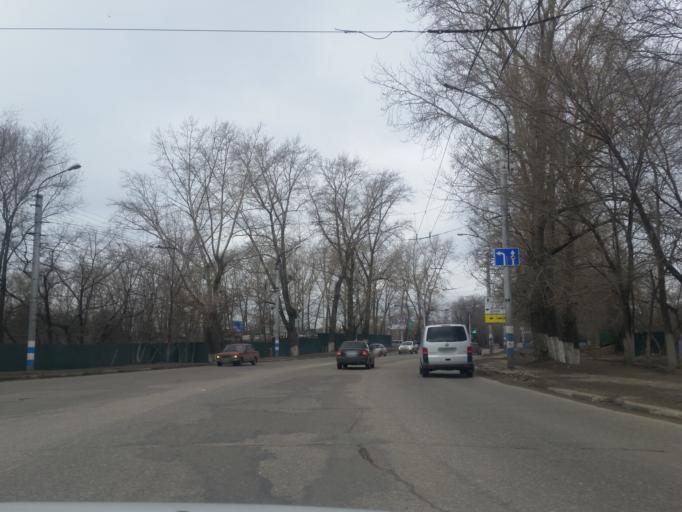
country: RU
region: Ulyanovsk
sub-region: Ulyanovskiy Rayon
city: Ulyanovsk
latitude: 54.3297
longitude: 48.4975
